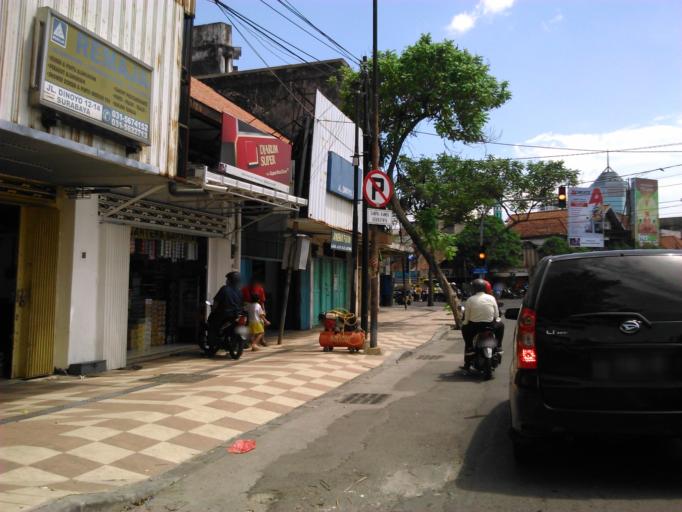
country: ID
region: East Java
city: Gubengairlangga
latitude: -7.2782
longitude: 112.7433
